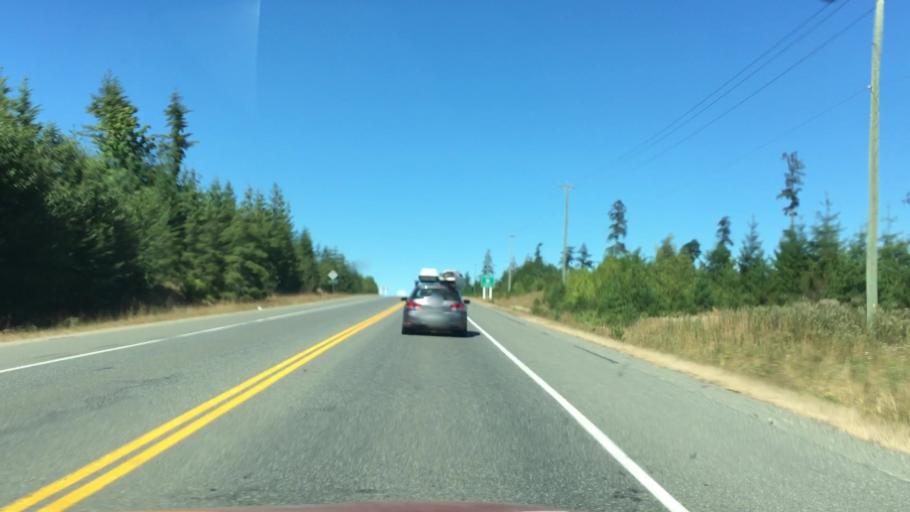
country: CA
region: British Columbia
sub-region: Regional District of Nanaimo
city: Parksville
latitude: 49.3175
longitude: -124.4447
